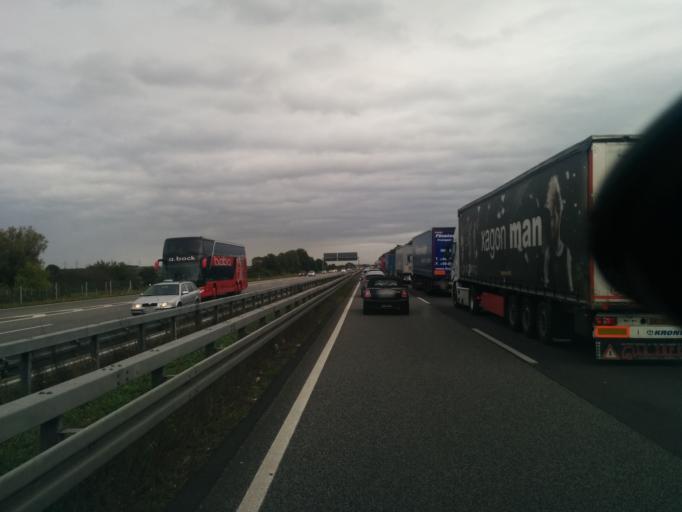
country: DE
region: North Rhine-Westphalia
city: Meckenheim
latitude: 50.5902
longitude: 7.0377
